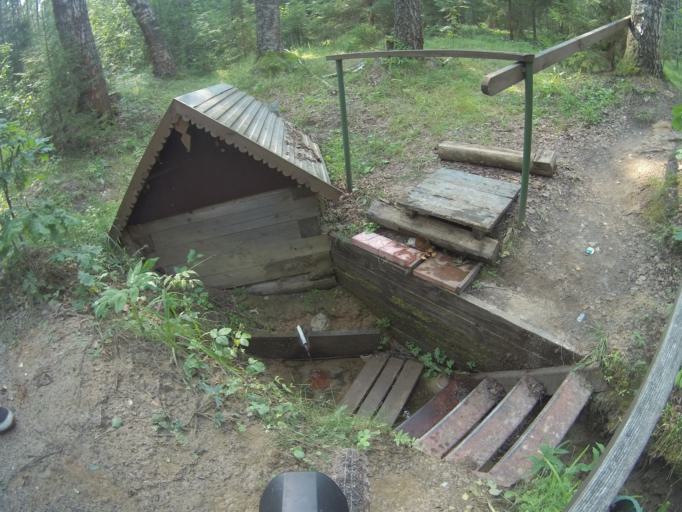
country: RU
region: Vladimir
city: Vorsha
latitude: 55.9783
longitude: 40.1603
